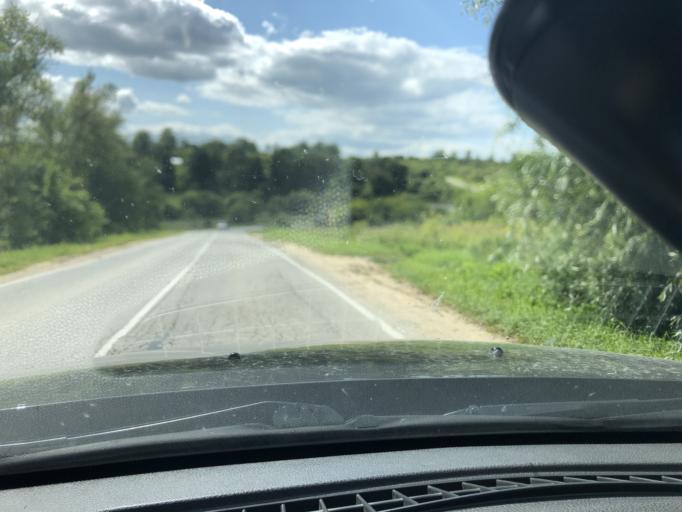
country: RU
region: Tula
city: Revyakino
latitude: 54.3464
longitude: 37.6157
